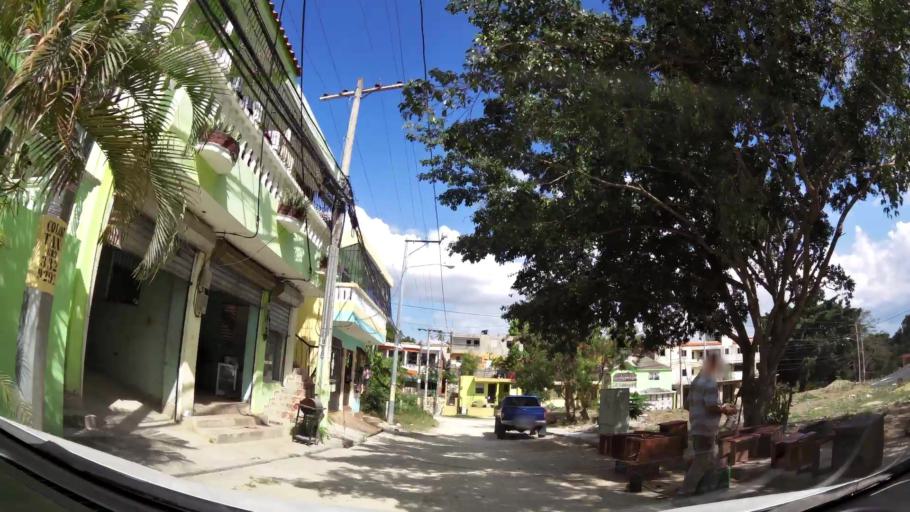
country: DO
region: Nacional
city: Ensanche Luperon
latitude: 18.5318
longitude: -69.8958
